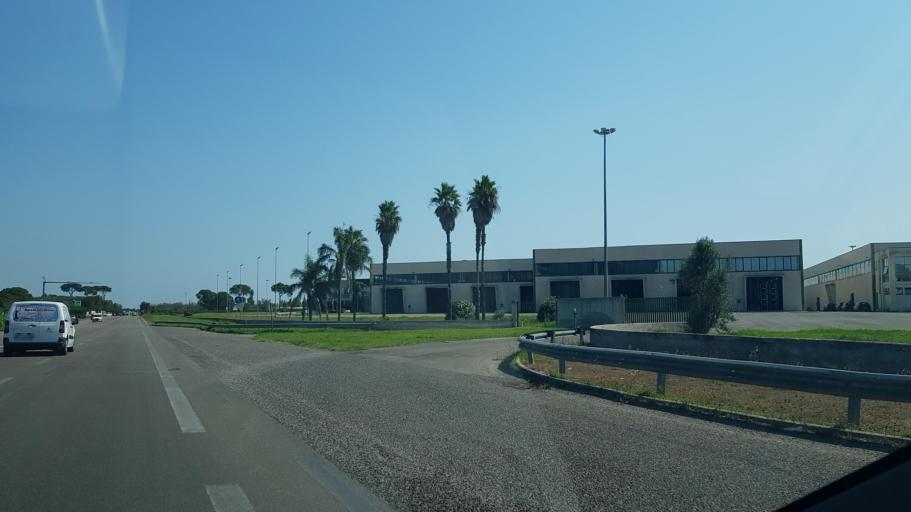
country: IT
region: Apulia
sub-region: Provincia di Lecce
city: Scorrano
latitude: 40.0983
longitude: 18.3142
